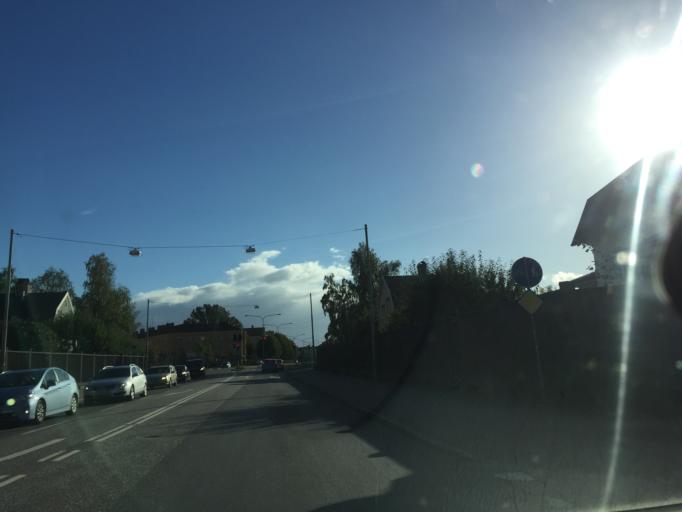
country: SE
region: OErebro
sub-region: Orebro Kommun
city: Orebro
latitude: 59.2858
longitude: 15.2036
